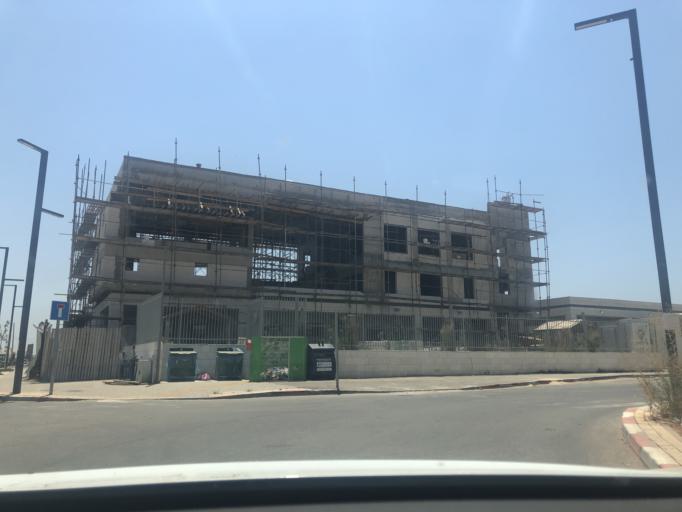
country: IL
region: Central District
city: Lod
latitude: 31.9341
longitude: 34.8987
